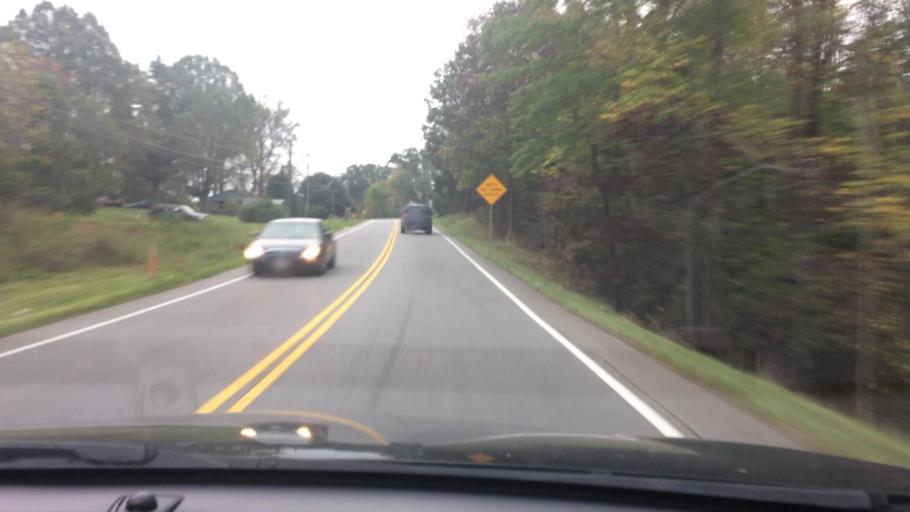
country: US
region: Virginia
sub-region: Franklin County
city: Henry Fork
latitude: 37.0165
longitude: -79.8306
